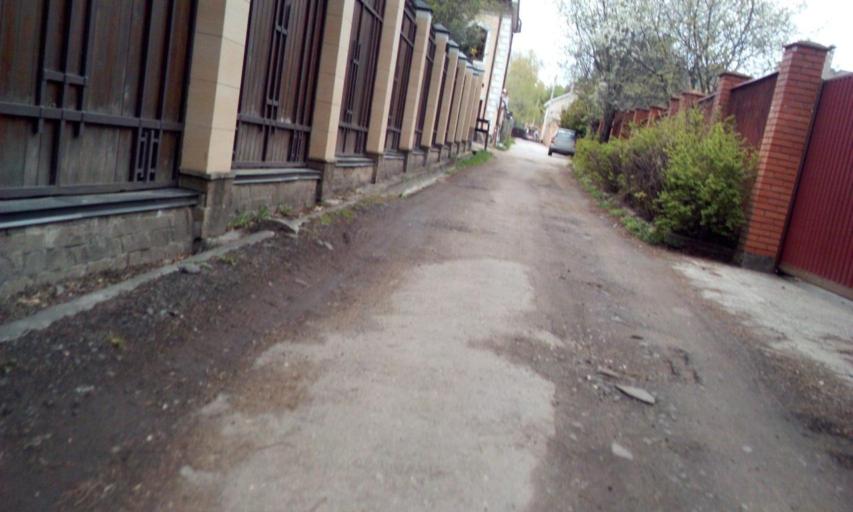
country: RU
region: Moskovskaya
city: Skolkovo
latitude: 55.6730
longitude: 37.3466
